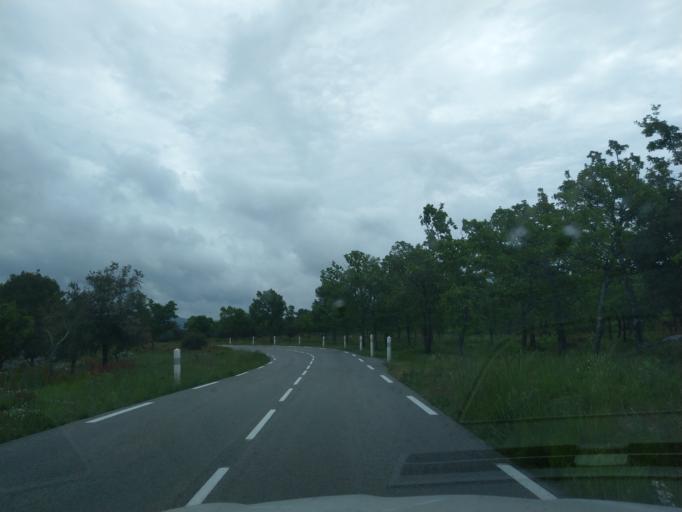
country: FR
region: Provence-Alpes-Cote d'Azur
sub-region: Departement du Var
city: Le Castellet
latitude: 43.2708
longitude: 5.7900
